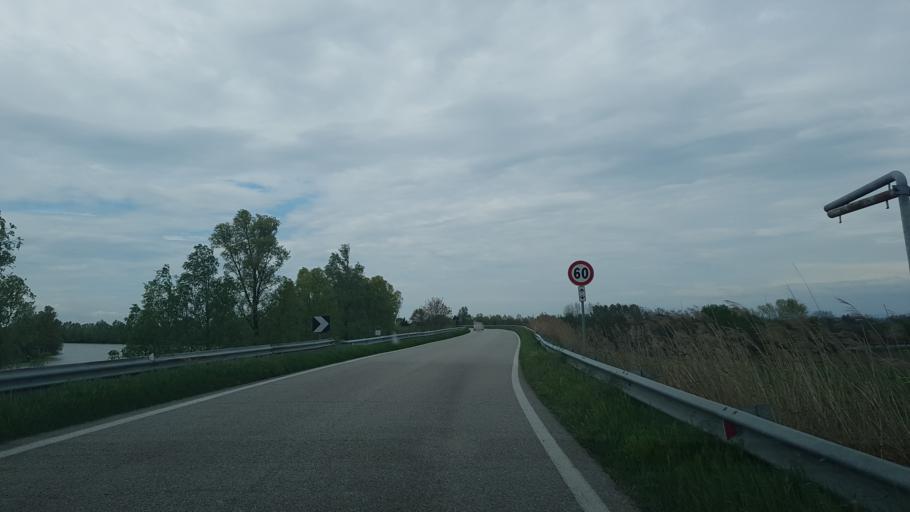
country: IT
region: Veneto
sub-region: Provincia di Rovigo
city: Lusia
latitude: 45.1091
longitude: 11.6325
